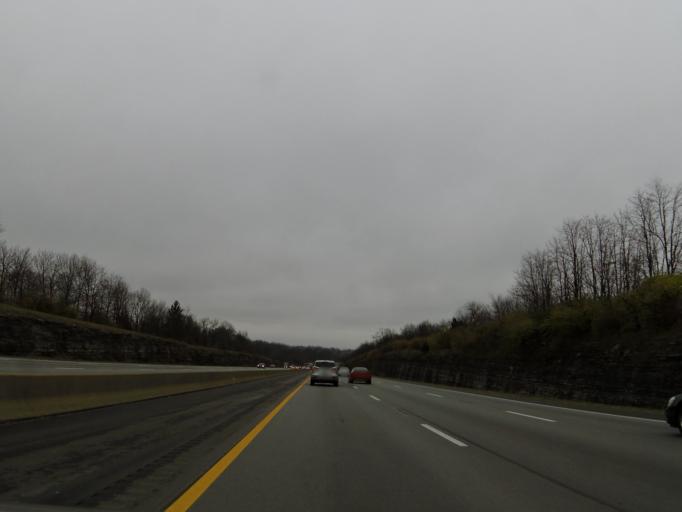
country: US
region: Kentucky
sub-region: Scott County
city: Georgetown
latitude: 38.2010
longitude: -84.5277
